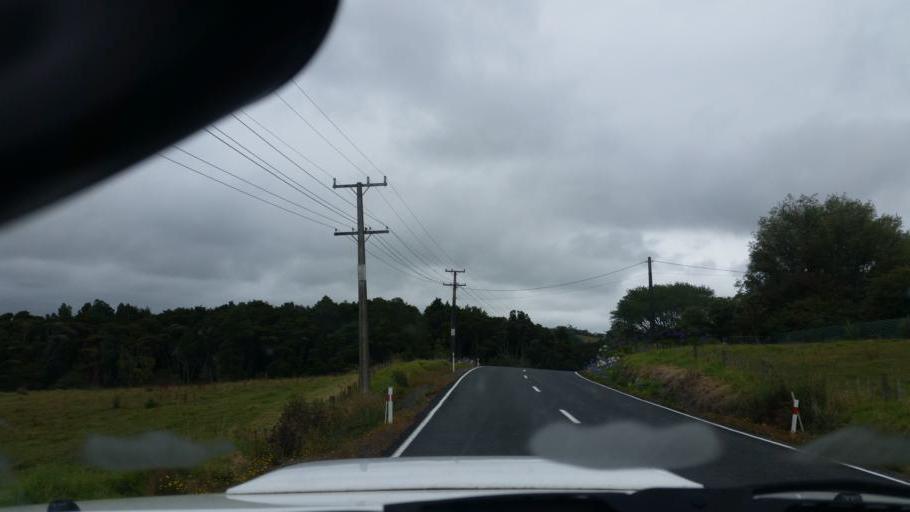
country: NZ
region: Auckland
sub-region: Auckland
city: Wellsford
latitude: -36.1574
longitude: 174.4602
